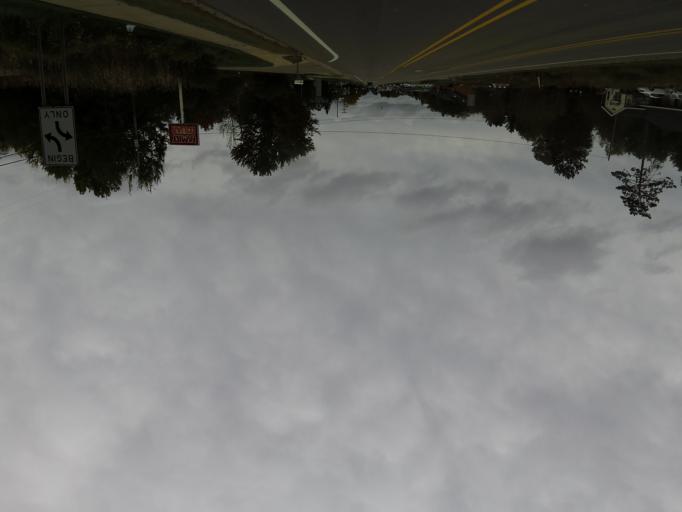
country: US
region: Michigan
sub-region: Roscommon County
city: Roscommon
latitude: 44.5030
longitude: -84.6001
